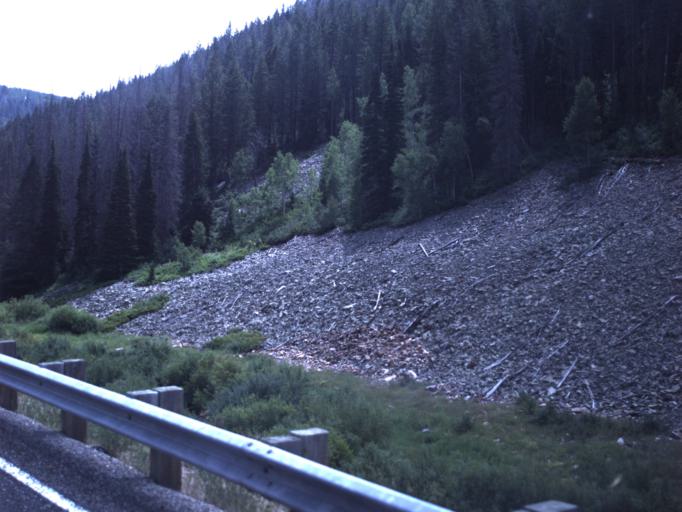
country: US
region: Utah
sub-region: Summit County
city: Francis
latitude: 40.5176
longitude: -111.0795
